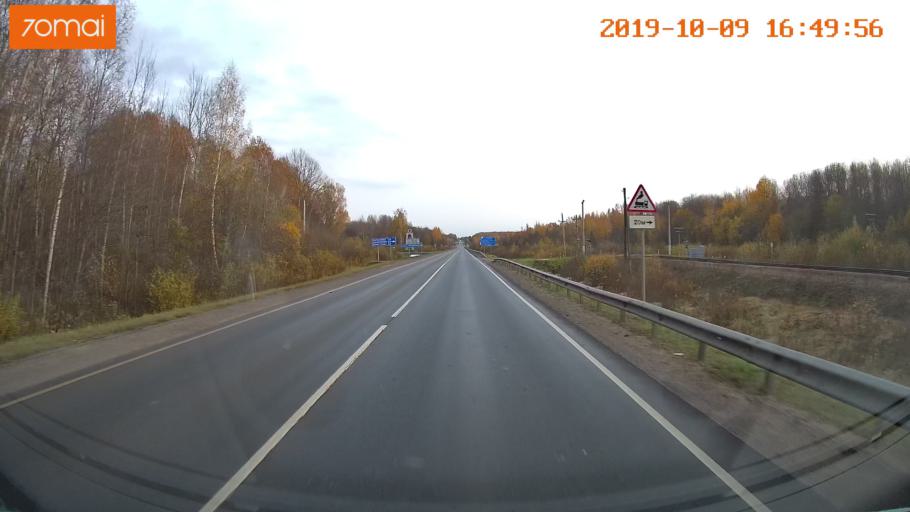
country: RU
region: Kostroma
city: Volgorechensk
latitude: 57.4080
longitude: 41.2023
